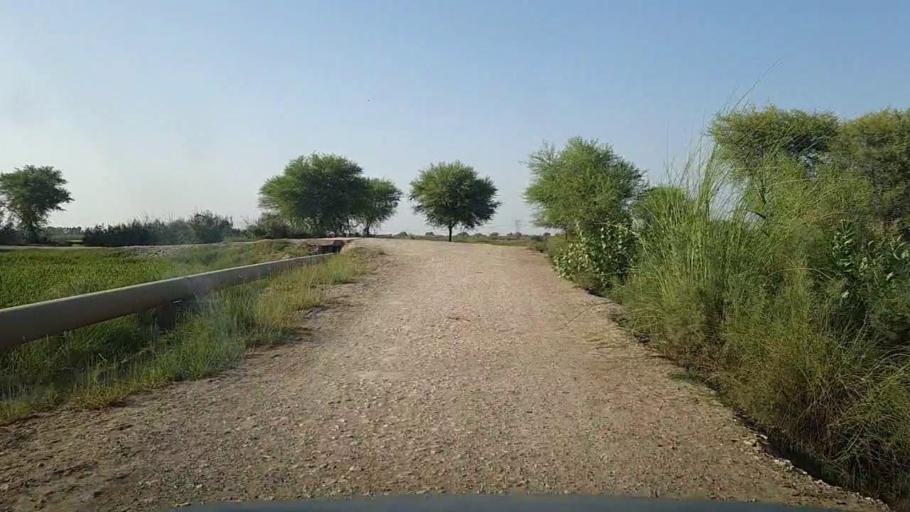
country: PK
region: Sindh
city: Kandhkot
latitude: 28.2884
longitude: 69.3322
